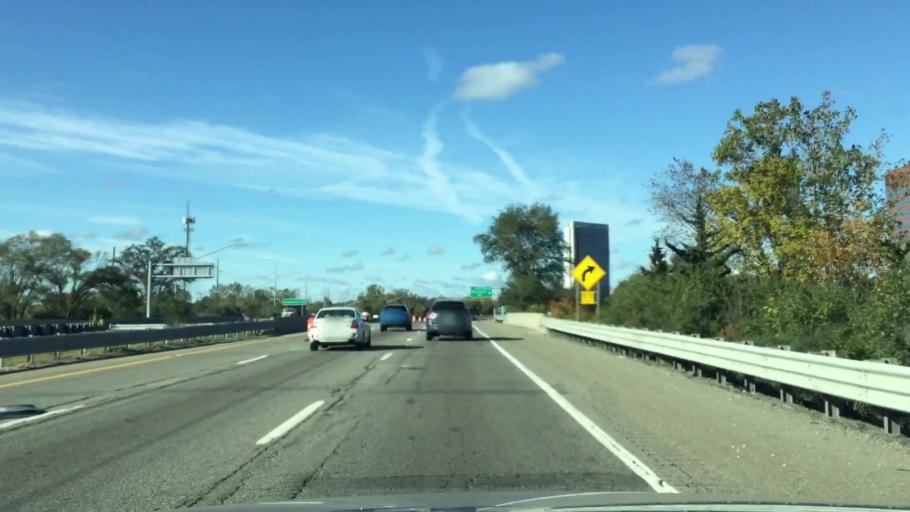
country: US
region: Michigan
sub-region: Oakland County
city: Clawson
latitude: 42.5592
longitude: -83.1467
